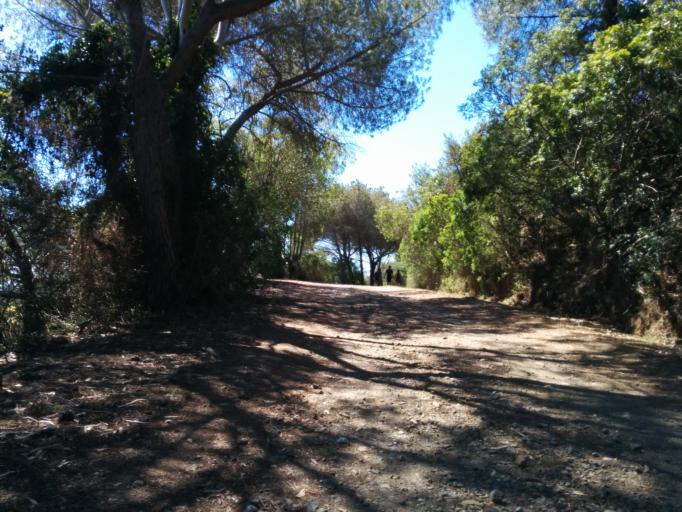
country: IT
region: Tuscany
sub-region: Provincia di Livorno
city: Portoferraio
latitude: 42.7537
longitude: 10.3190
